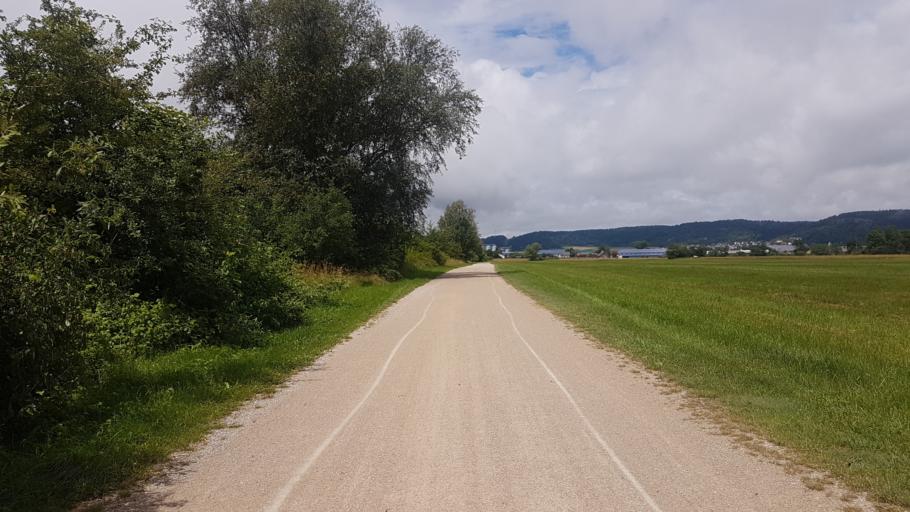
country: DE
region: Bavaria
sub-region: Upper Palatinate
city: Dietfurt
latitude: 49.0171
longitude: 11.5989
